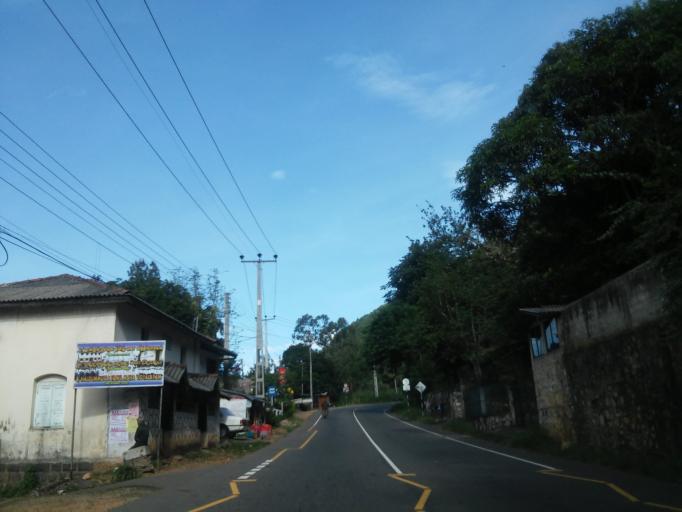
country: LK
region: Uva
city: Haputale
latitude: 6.7652
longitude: 80.8924
